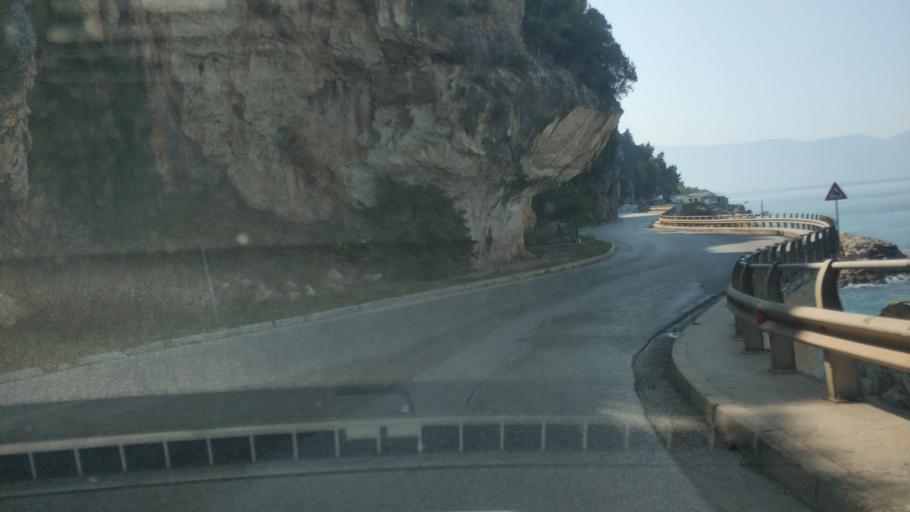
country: AL
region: Vlore
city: Vlore
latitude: 40.4127
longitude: 19.4811
